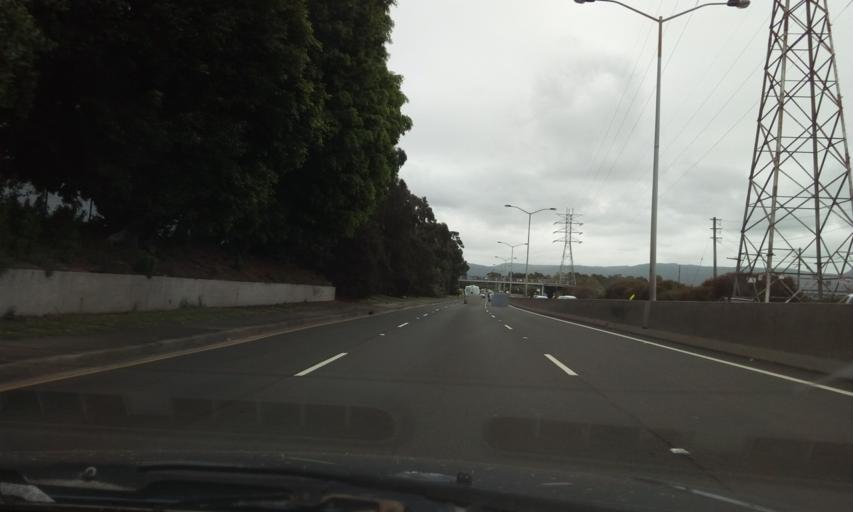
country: AU
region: New South Wales
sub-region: Wollongong
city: Cringila
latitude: -34.4691
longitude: 150.8807
